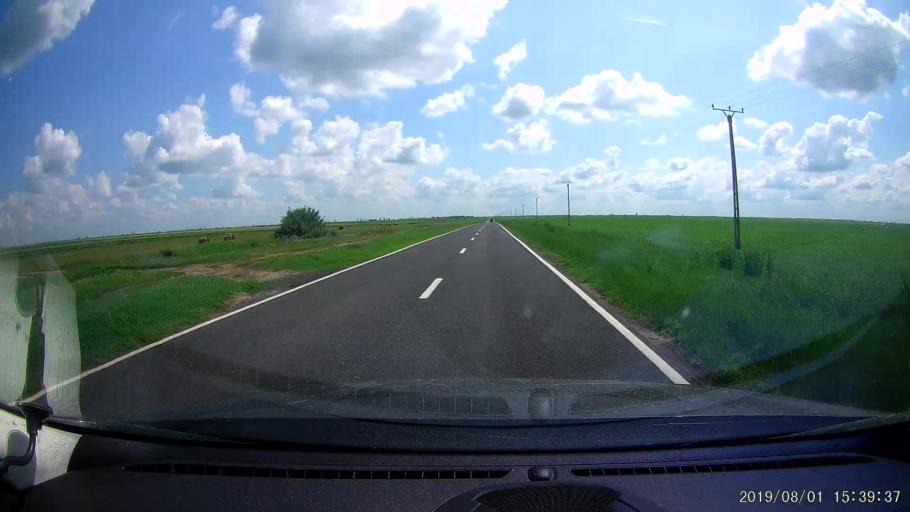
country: RO
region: Braila
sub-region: Comuna Baraganul
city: Baraganul
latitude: 44.8535
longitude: 27.5561
